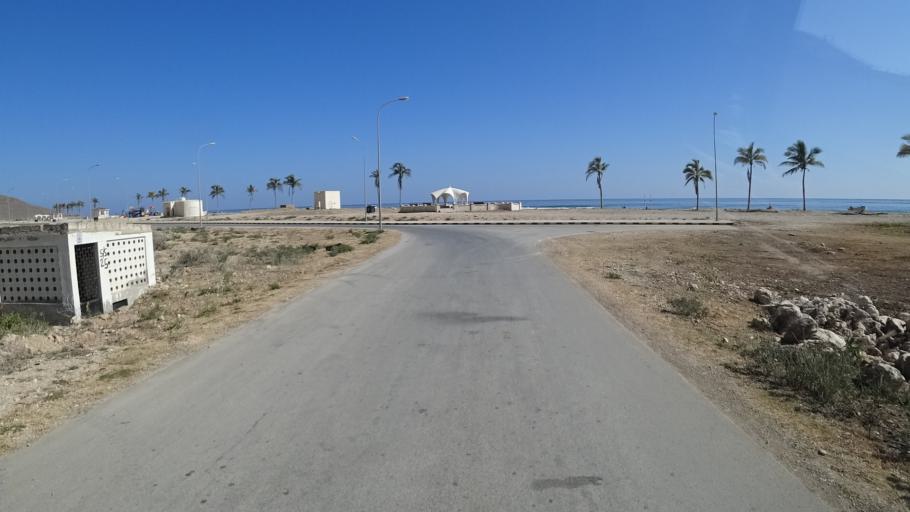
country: YE
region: Al Mahrah
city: Hawf
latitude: 16.7477
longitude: 53.4268
